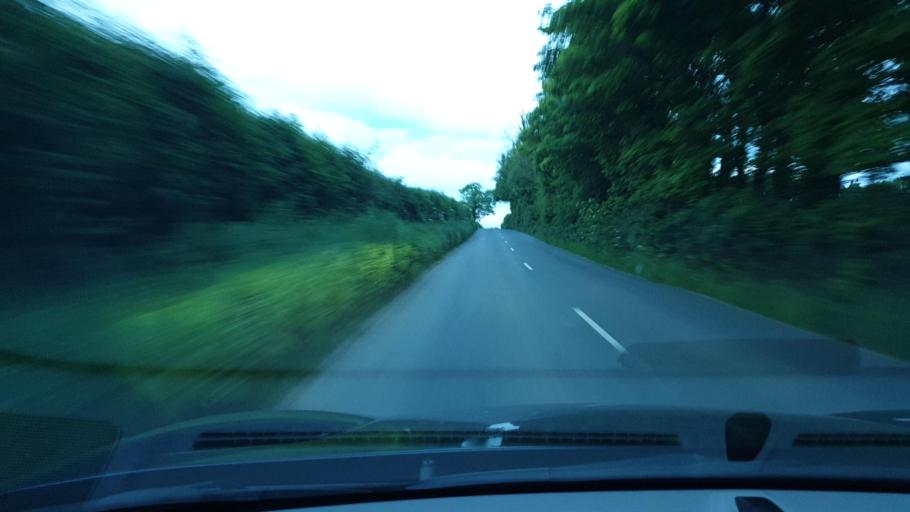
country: IE
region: Leinster
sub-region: An Mhi
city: Ashbourne
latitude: 53.5668
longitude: -6.4293
